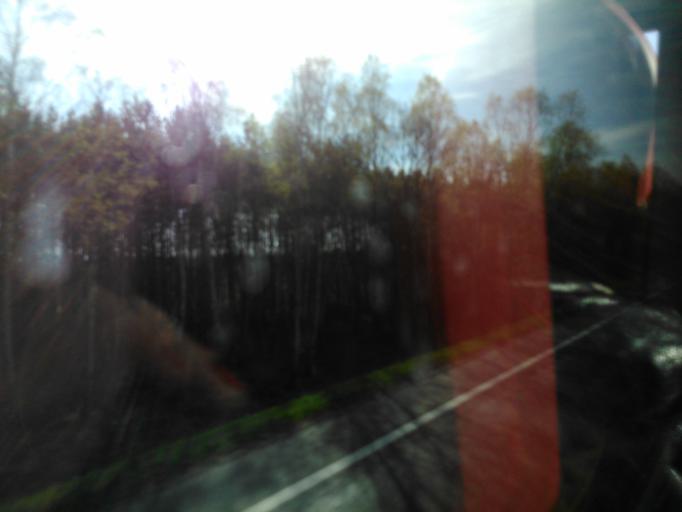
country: PL
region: Kujawsko-Pomorskie
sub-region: Powiat aleksandrowski
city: Aleksandrow Kujawski
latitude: 52.9641
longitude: 18.6842
